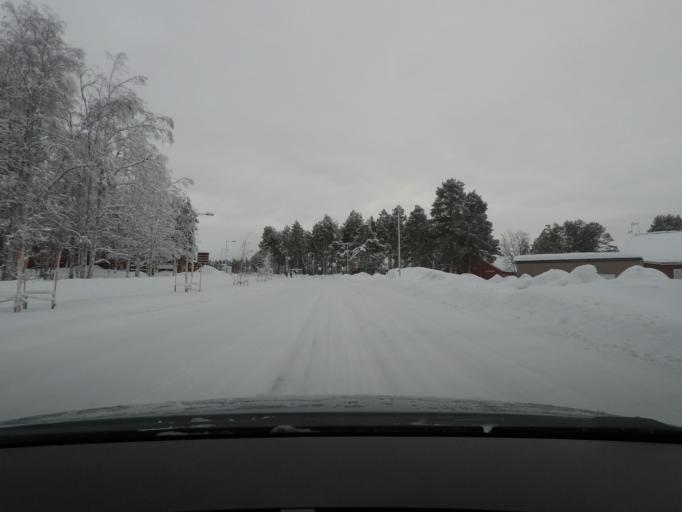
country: SE
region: Norrbotten
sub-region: Lulea Kommun
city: Lulea
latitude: 65.5930
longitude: 22.1885
